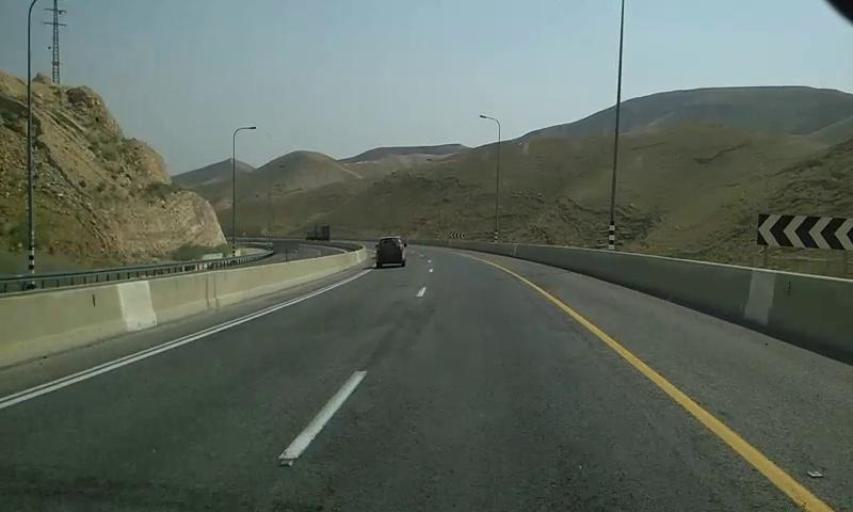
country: PS
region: West Bank
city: Jericho
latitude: 31.8105
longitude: 35.3908
